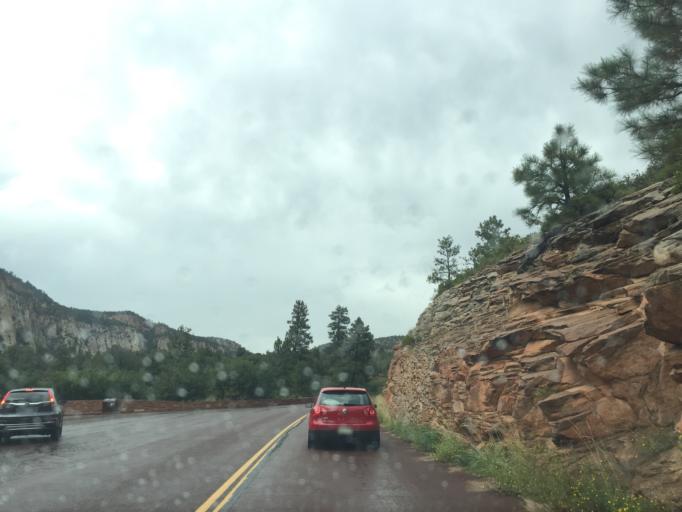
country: US
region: Utah
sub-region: Washington County
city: Hildale
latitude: 37.2301
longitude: -112.8786
